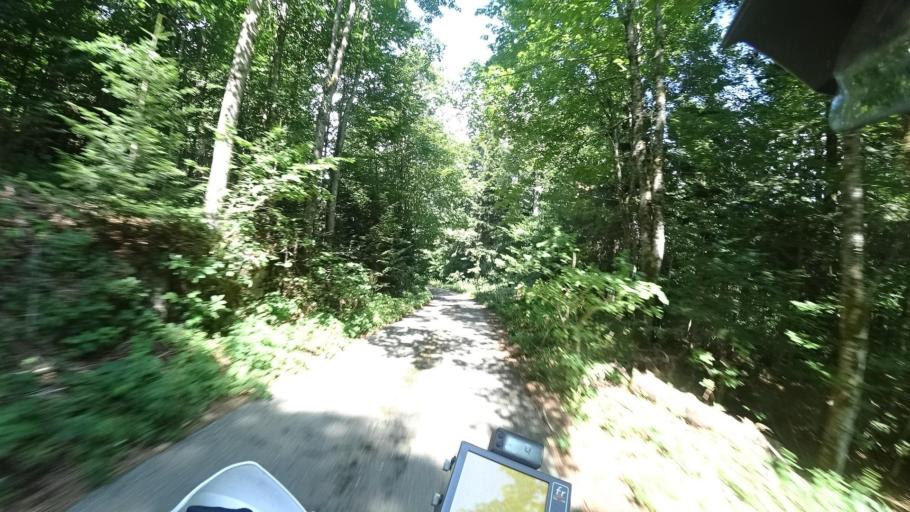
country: HR
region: Licko-Senjska
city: Brinje
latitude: 45.1103
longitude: 15.0361
